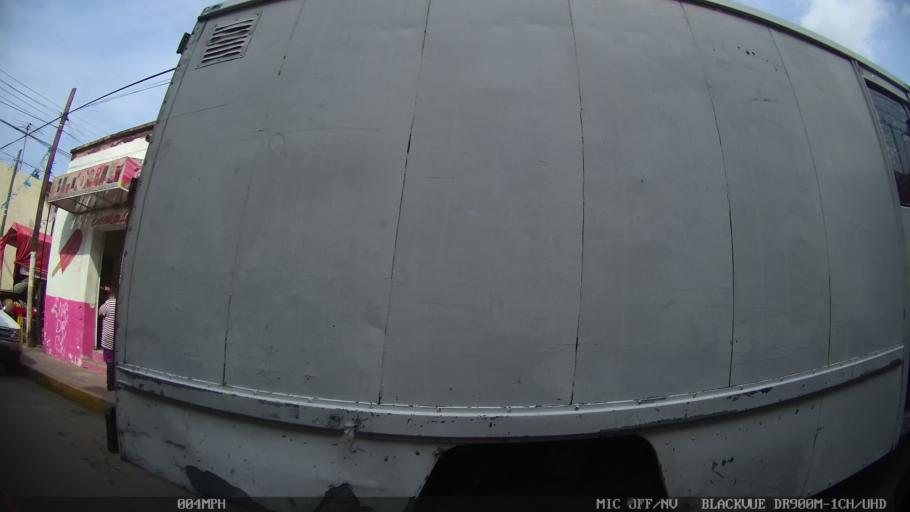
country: MX
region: Jalisco
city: Tonala
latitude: 20.6234
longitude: -103.2402
